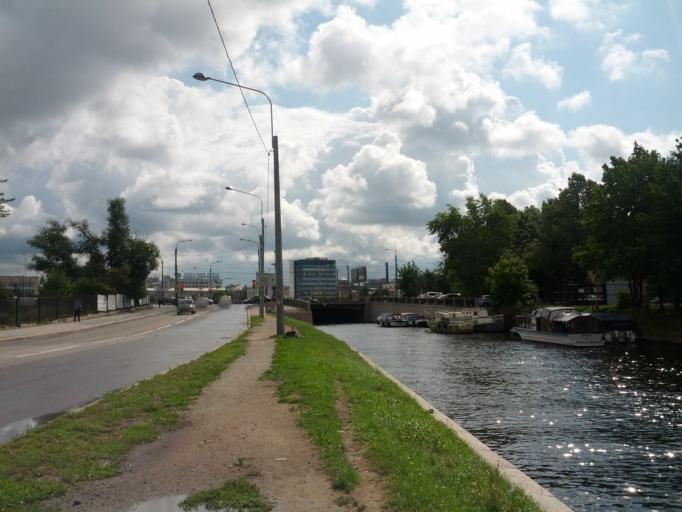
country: RU
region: St.-Petersburg
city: Petrogradka
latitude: 59.9679
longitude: 30.3294
